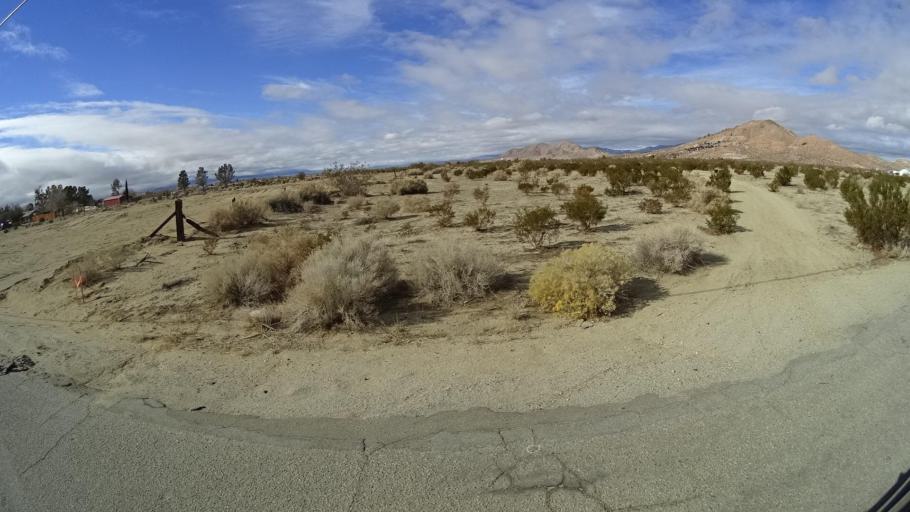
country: US
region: California
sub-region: Kern County
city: Rosamond
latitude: 34.8710
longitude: -118.2202
